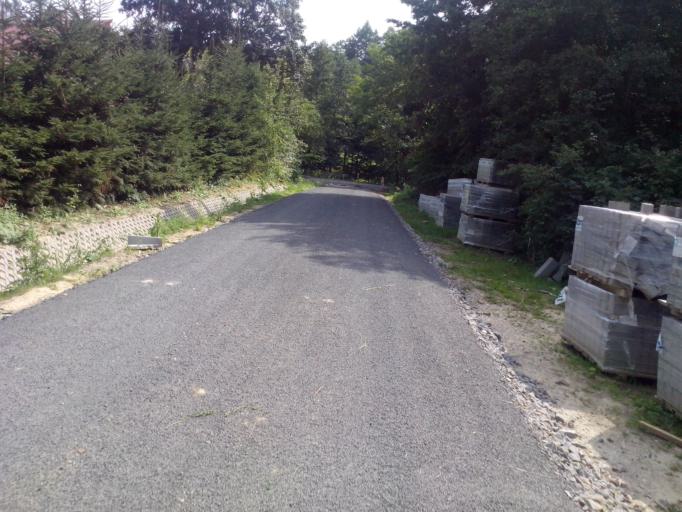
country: PL
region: Subcarpathian Voivodeship
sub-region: Powiat strzyzowski
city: Strzyzow
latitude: 49.7994
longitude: 21.8170
